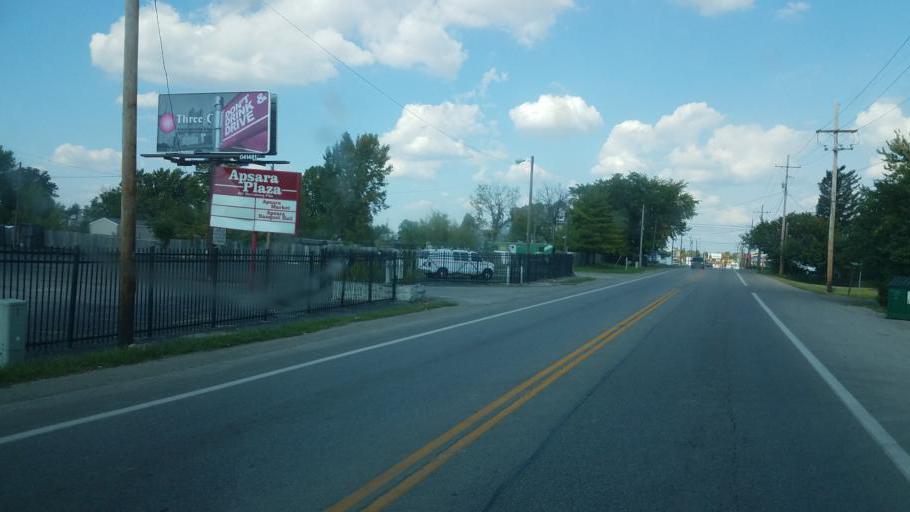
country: US
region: Ohio
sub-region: Franklin County
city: Grandview Heights
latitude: 39.9405
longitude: -83.0398
